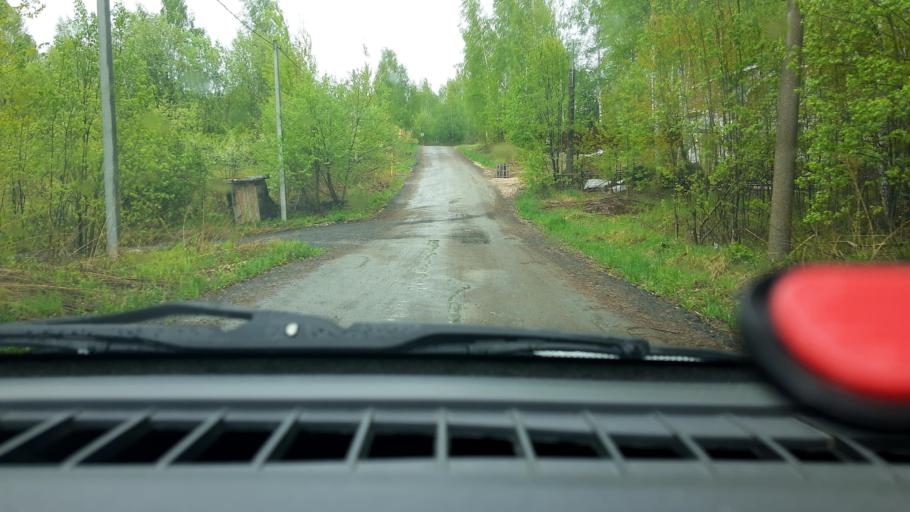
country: RU
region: Nizjnij Novgorod
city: Afonino
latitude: 56.2468
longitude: 44.0714
